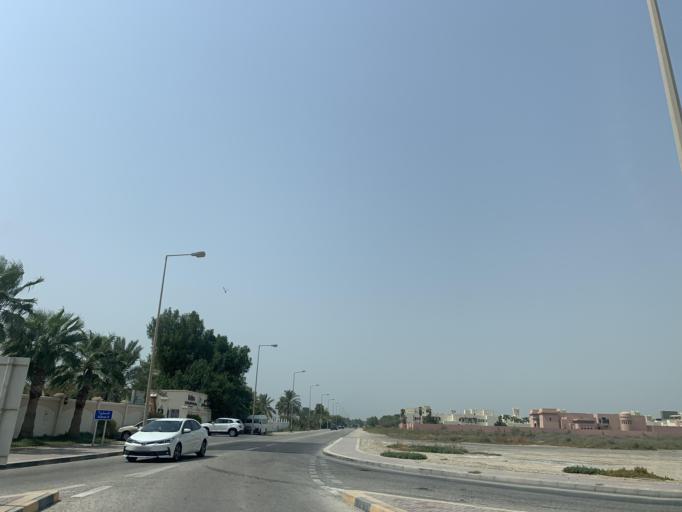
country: BH
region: Central Governorate
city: Madinat Hamad
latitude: 26.1573
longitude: 50.4668
